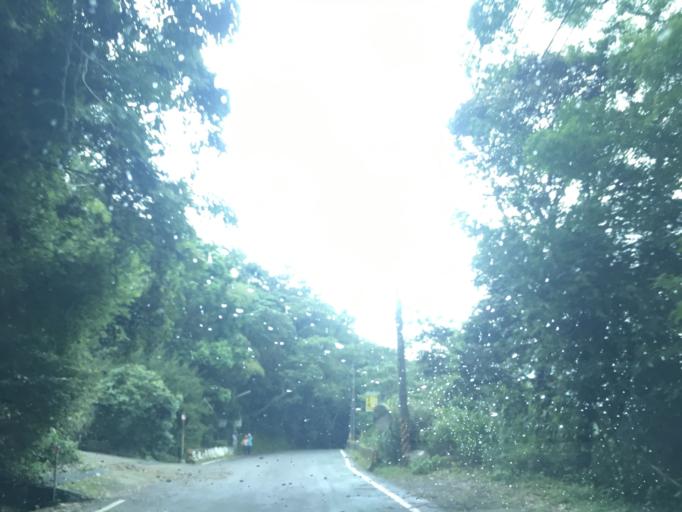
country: TW
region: Taiwan
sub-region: Yunlin
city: Douliu
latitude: 23.5620
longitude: 120.6114
